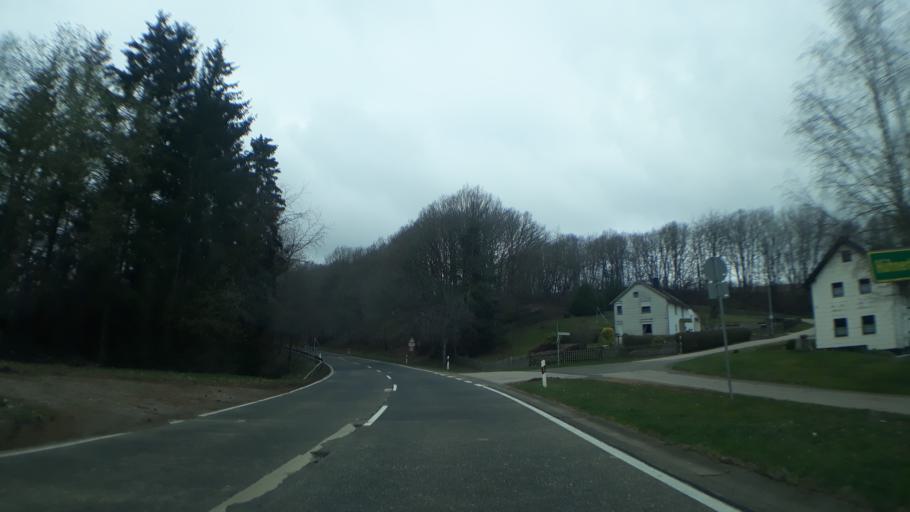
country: DE
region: North Rhine-Westphalia
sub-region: Regierungsbezirk Koln
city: Schleiden
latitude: 50.5518
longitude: 6.4683
